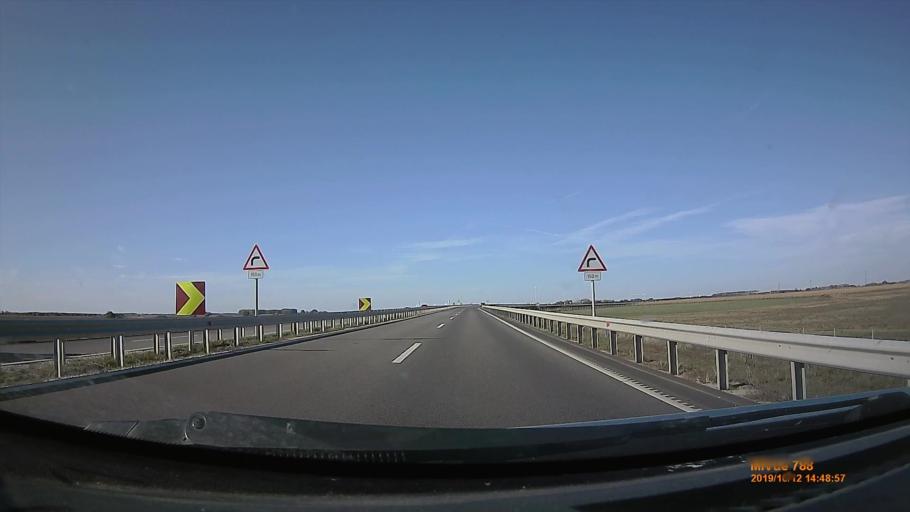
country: HU
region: Hajdu-Bihar
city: Derecske
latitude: 47.2948
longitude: 21.5049
